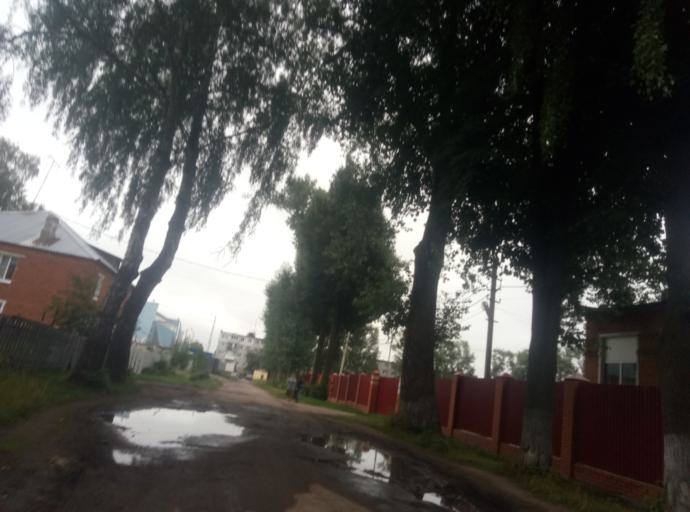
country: RU
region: Tula
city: Kireyevsk
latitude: 53.9250
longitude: 37.9280
